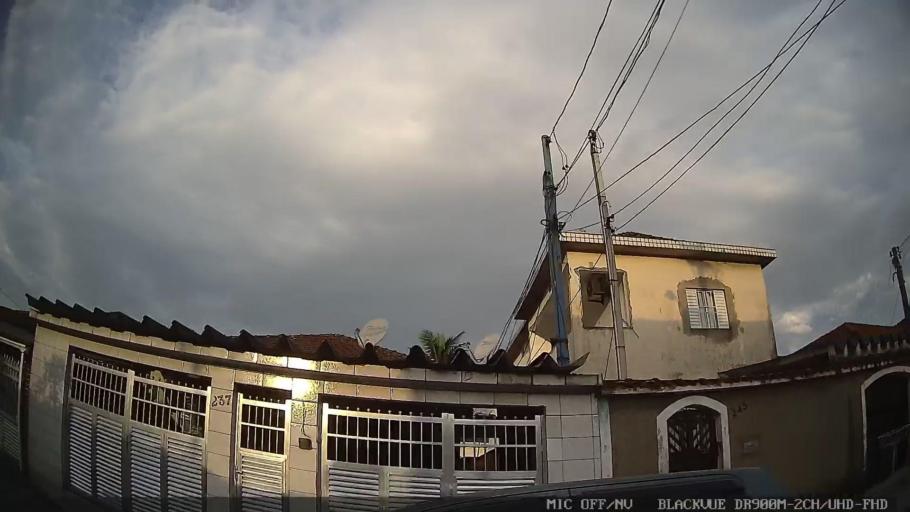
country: BR
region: Sao Paulo
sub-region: Cubatao
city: Cubatao
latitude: -23.8938
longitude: -46.4296
